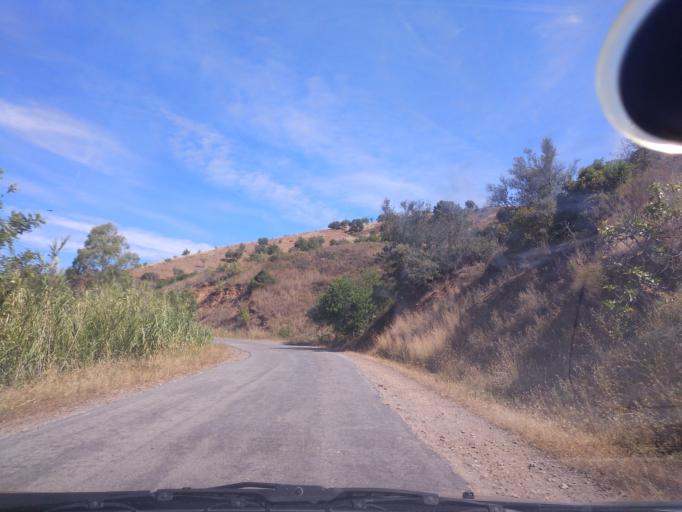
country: PT
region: Faro
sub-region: Olhao
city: Moncarapacho
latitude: 37.1631
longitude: -7.7988
